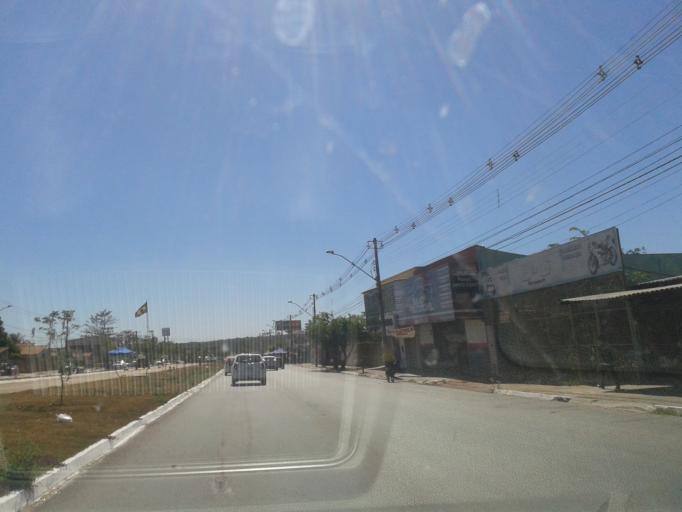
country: BR
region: Goias
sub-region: Goiania
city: Goiania
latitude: -16.6353
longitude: -49.2724
